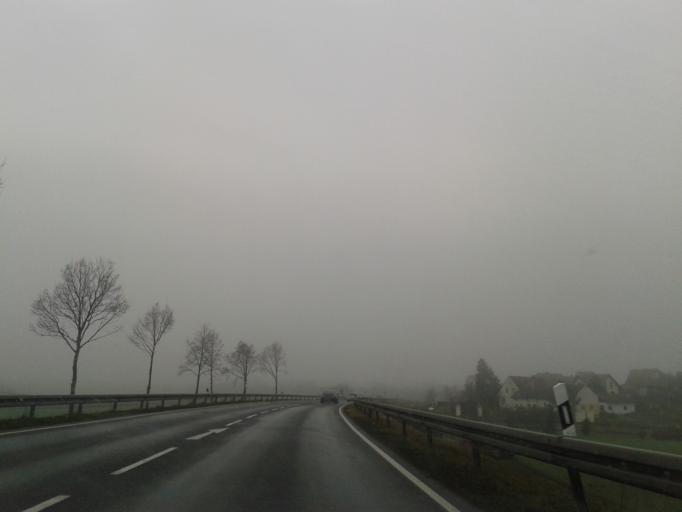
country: DE
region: Bavaria
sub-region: Upper Franconia
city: Sesslach
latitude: 50.2222
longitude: 10.8352
